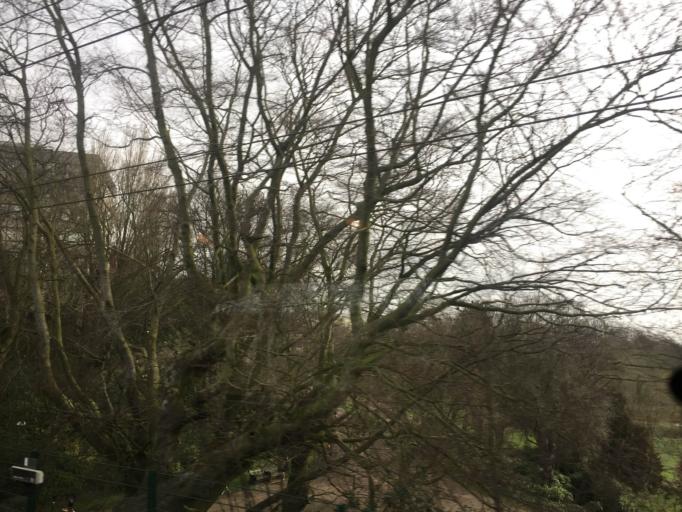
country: GB
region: England
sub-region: Lancashire
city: Preston
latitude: 53.7514
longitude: -2.7063
